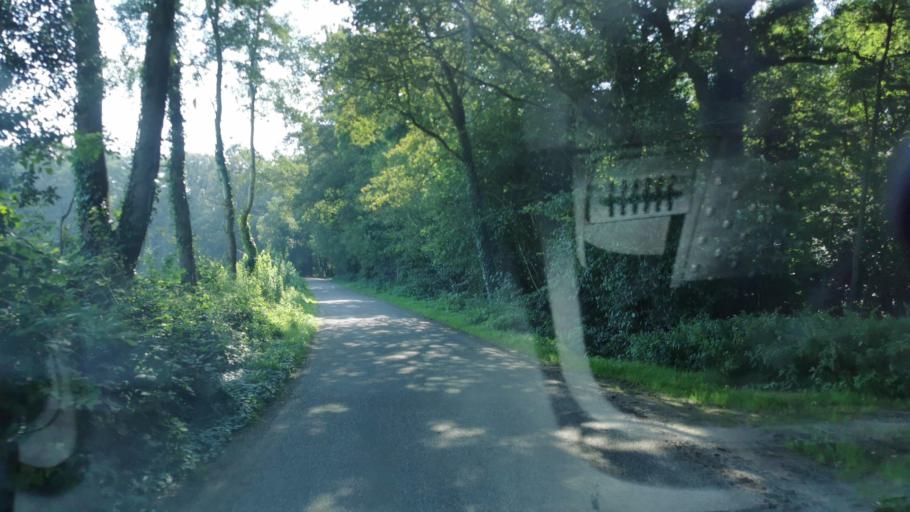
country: NL
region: Overijssel
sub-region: Gemeente Tubbergen
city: Tubbergen
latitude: 52.3485
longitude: 6.8137
